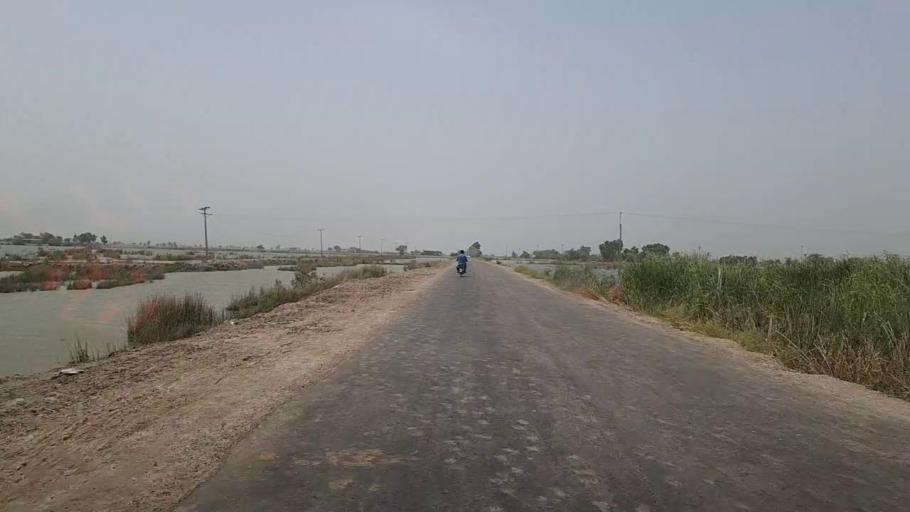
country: PK
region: Sindh
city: Radhan
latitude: 27.1487
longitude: 67.9377
